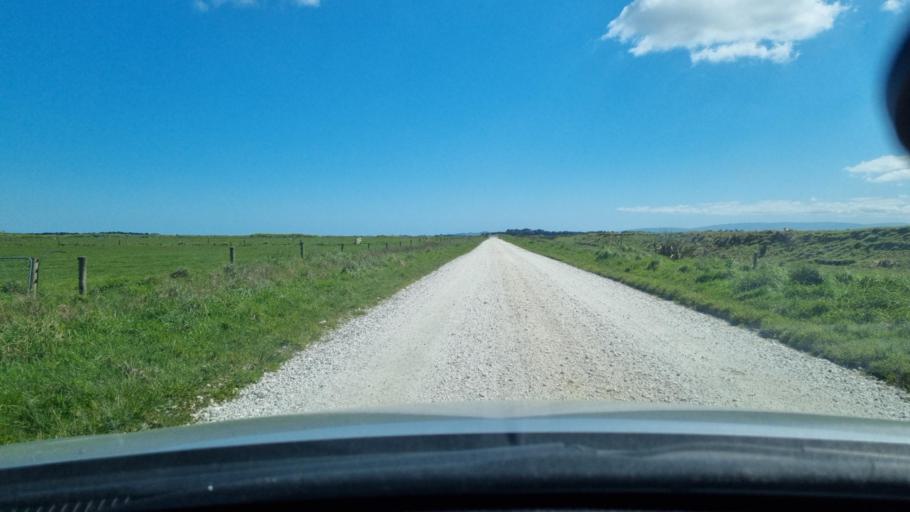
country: NZ
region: Southland
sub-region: Invercargill City
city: Invercargill
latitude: -46.3693
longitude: 168.2583
